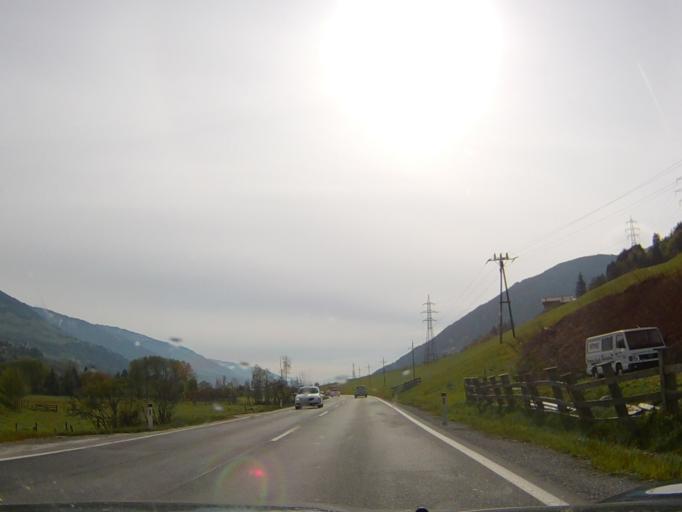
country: AT
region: Salzburg
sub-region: Politischer Bezirk Zell am See
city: Hollersbach im Pinzgau
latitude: 47.2764
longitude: 12.4467
